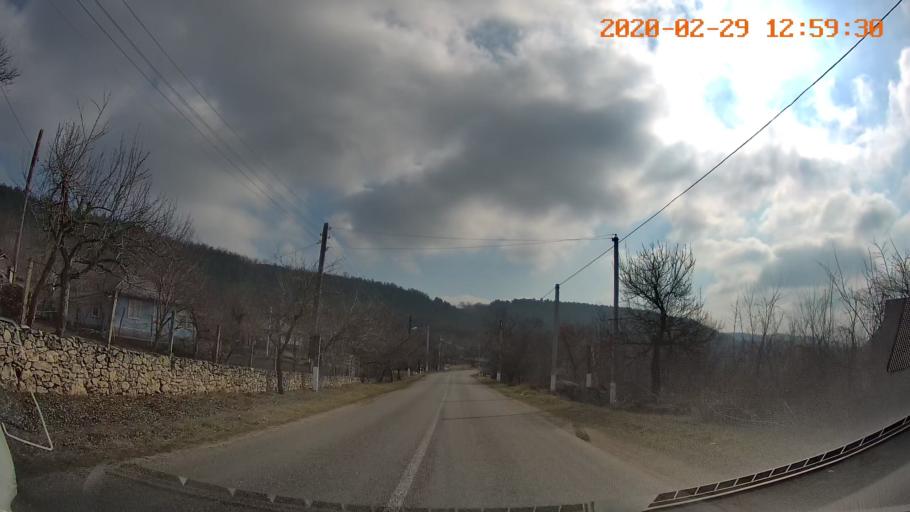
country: MD
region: Telenesti
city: Camenca
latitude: 48.0615
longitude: 28.7243
